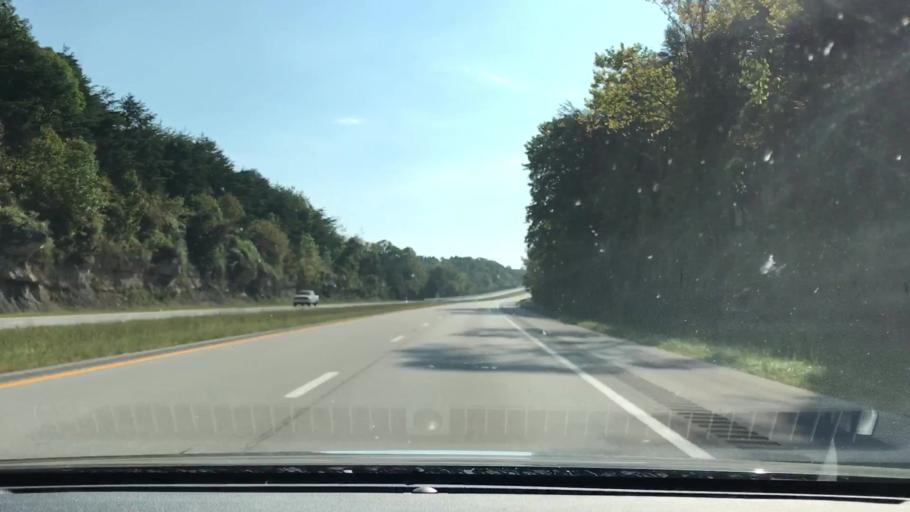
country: US
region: Kentucky
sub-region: Pulaski County
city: Somerset
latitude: 37.0970
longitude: -84.8308
